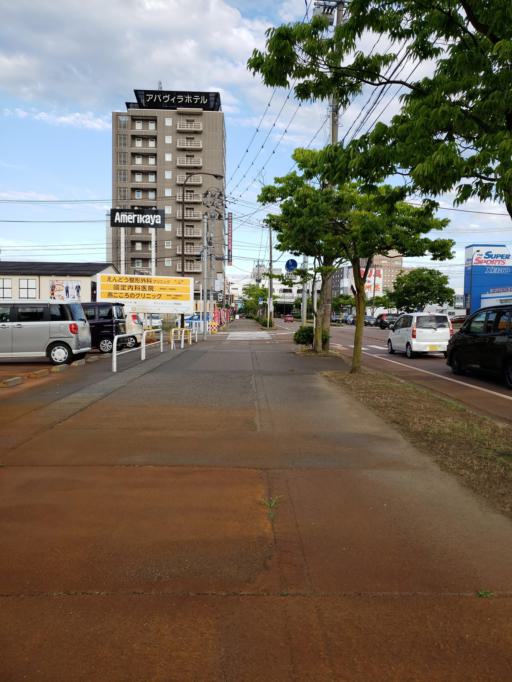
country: JP
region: Niigata
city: Tsubame
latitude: 37.6496
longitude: 138.9358
